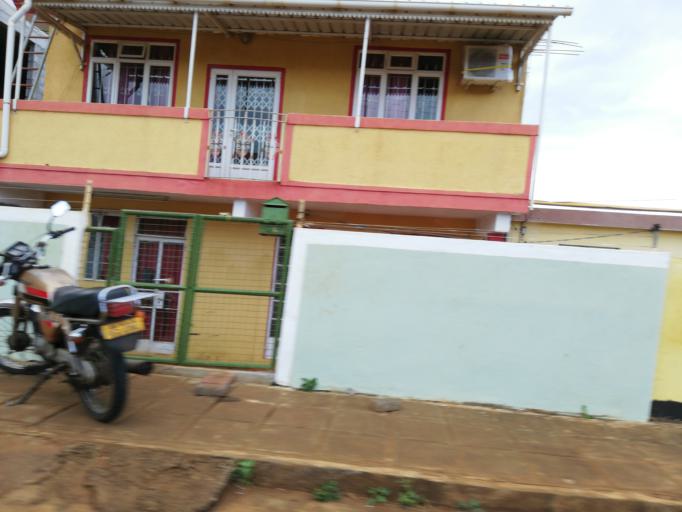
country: MU
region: Black River
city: Petite Riviere
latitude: -20.2122
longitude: 57.4627
